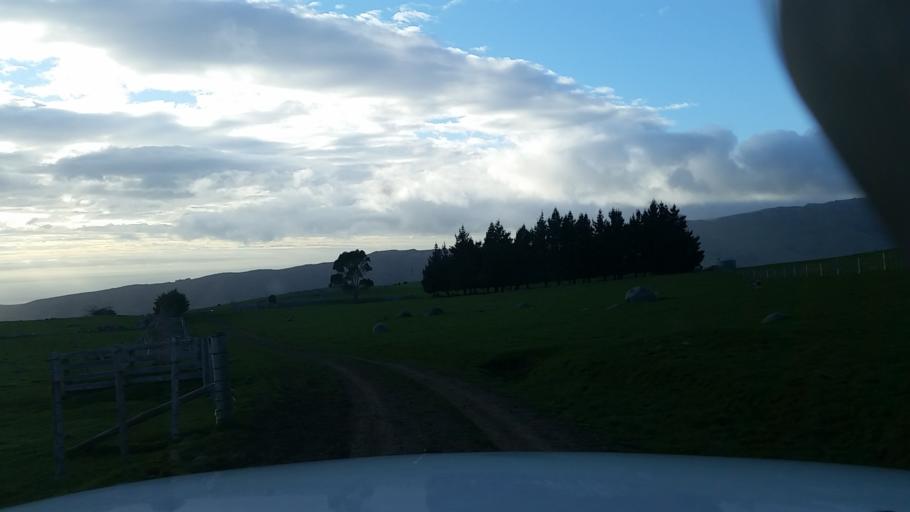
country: NZ
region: Canterbury
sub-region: Christchurch City
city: Christchurch
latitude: -43.6584
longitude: 172.8713
